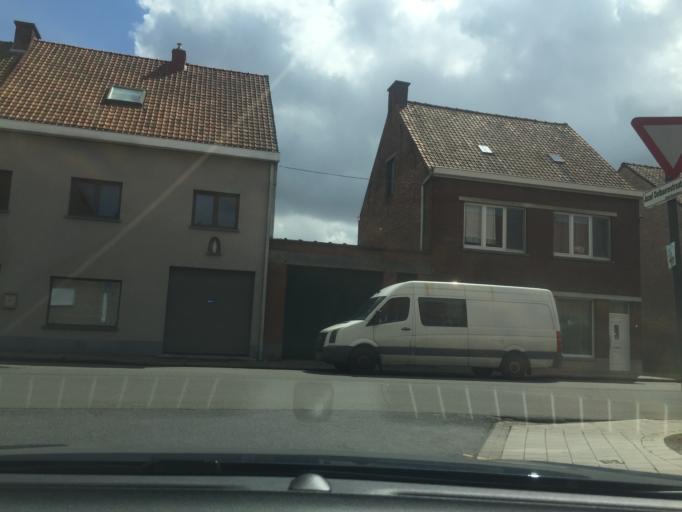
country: BE
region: Flanders
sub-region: Provincie West-Vlaanderen
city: Roeselare
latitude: 50.9315
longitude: 3.1478
